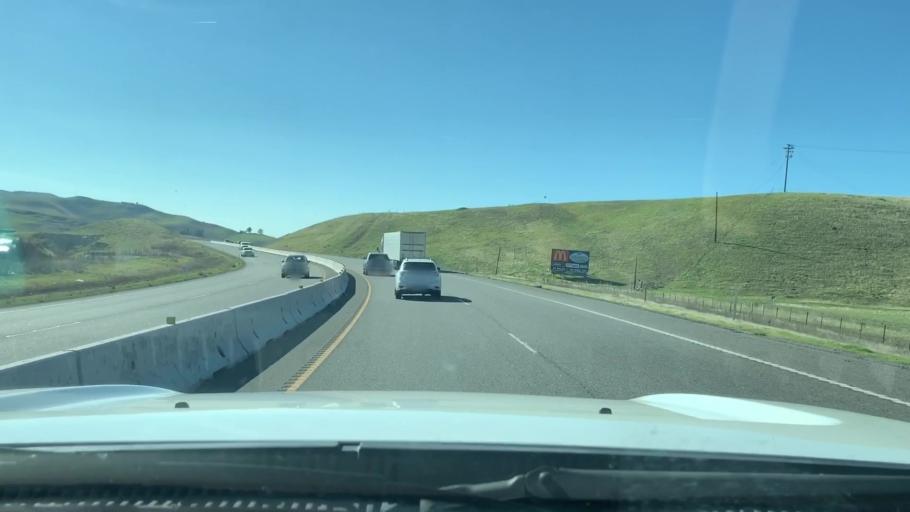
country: US
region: California
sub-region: San Luis Obispo County
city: Shandon
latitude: 35.7034
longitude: -120.3221
